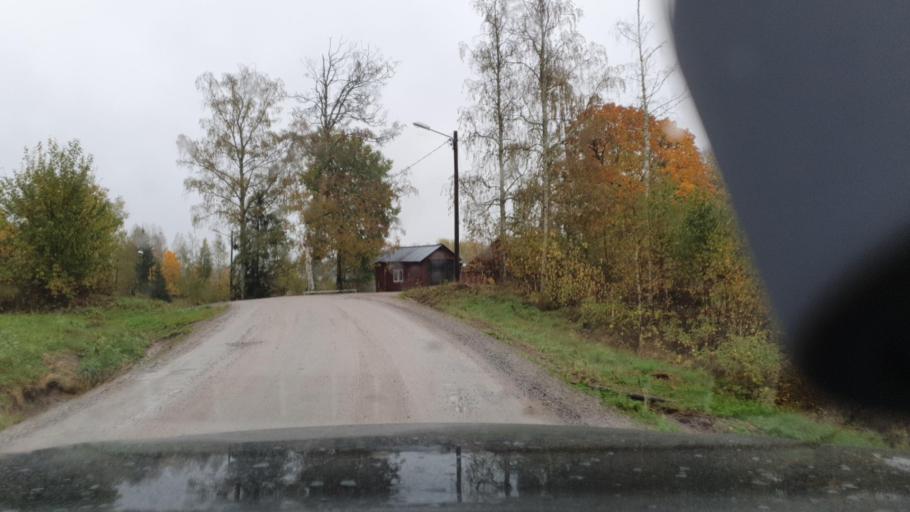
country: SE
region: Vaermland
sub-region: Arvika Kommun
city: Arvika
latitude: 59.6111
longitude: 12.9064
